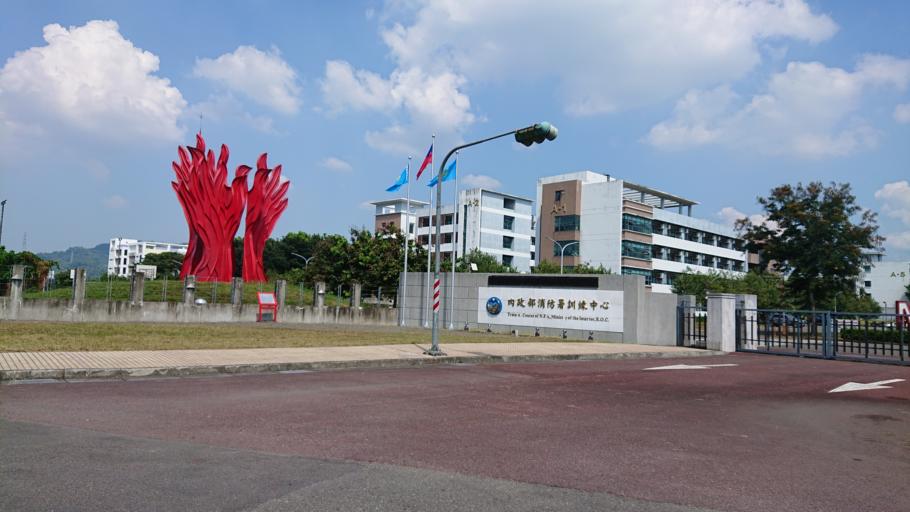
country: TW
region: Taiwan
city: Lugu
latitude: 23.8172
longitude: 120.7180
